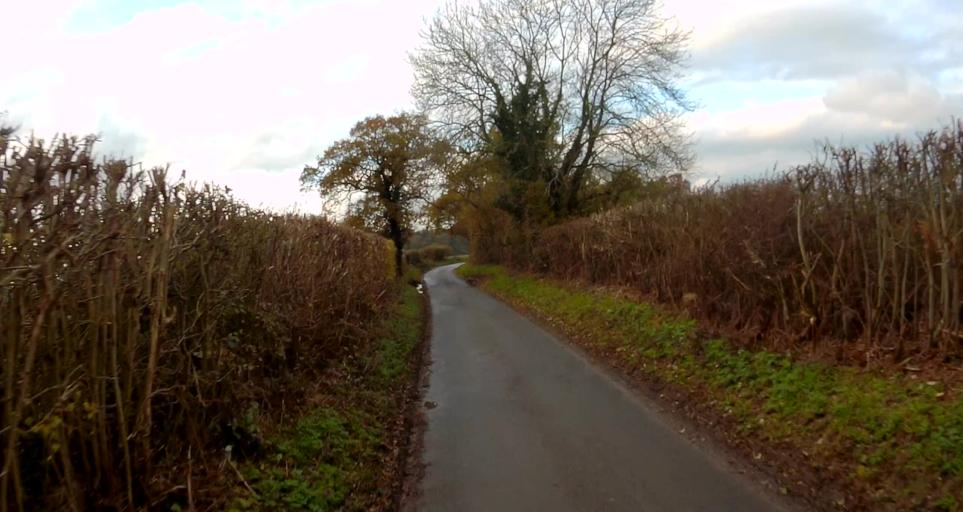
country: GB
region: England
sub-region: Hampshire
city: Long Sutton
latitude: 51.2092
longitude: -0.9411
